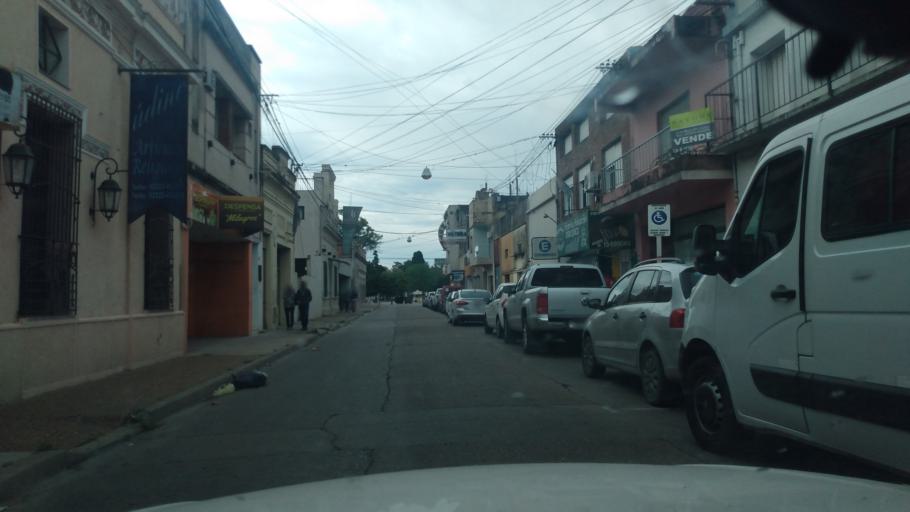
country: AR
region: Buenos Aires
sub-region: Partido de Lujan
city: Lujan
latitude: -34.5632
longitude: -59.1192
